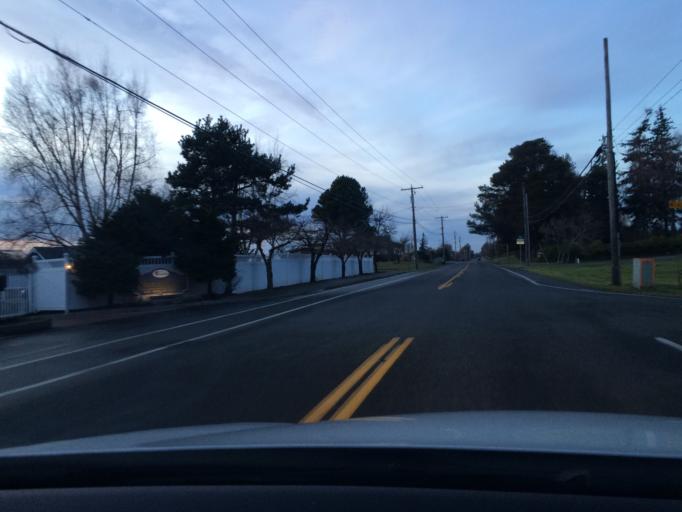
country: US
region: Washington
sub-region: Whatcom County
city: Marietta-Alderwood
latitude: 48.7744
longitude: -122.5304
